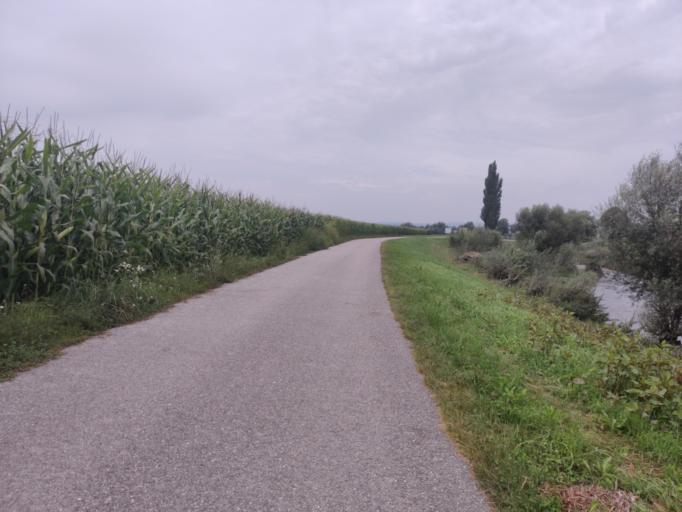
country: AT
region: Lower Austria
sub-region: Politischer Bezirk Amstetten
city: Strengberg
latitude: 48.1834
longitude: 14.7205
